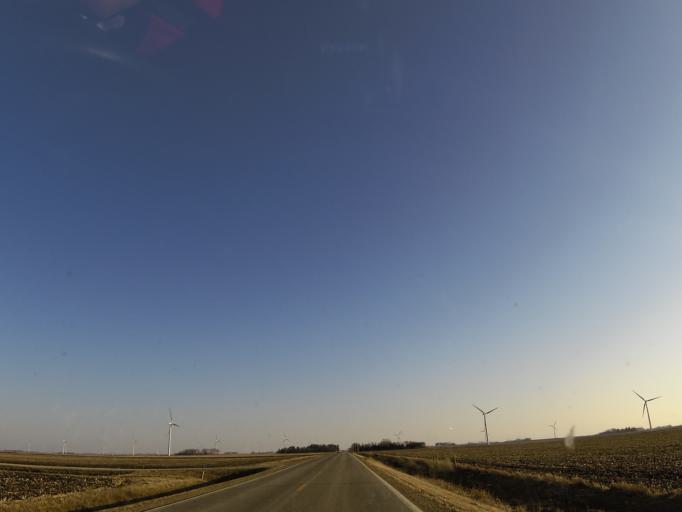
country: US
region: Iowa
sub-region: Worth County
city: Northwood
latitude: 43.4197
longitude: -93.1244
